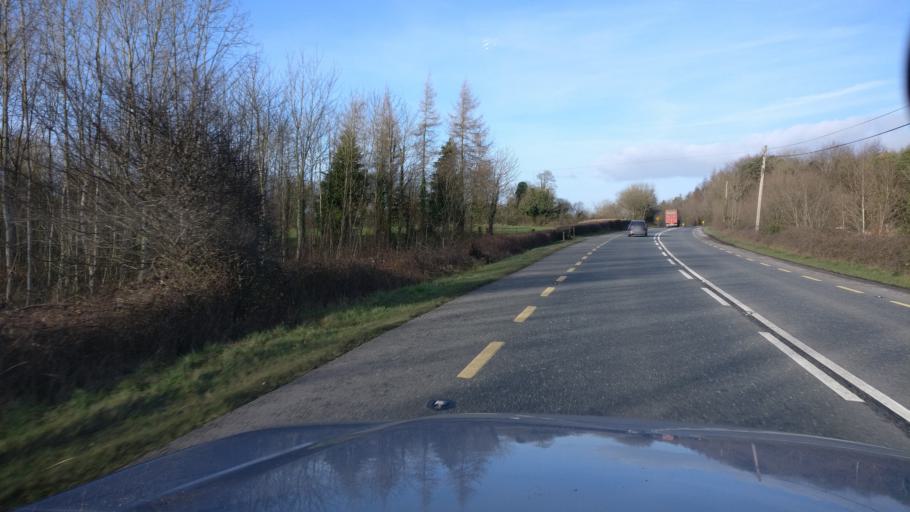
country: IE
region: Leinster
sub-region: Uibh Fhaili
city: Tullamore
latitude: 53.2271
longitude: -7.4759
